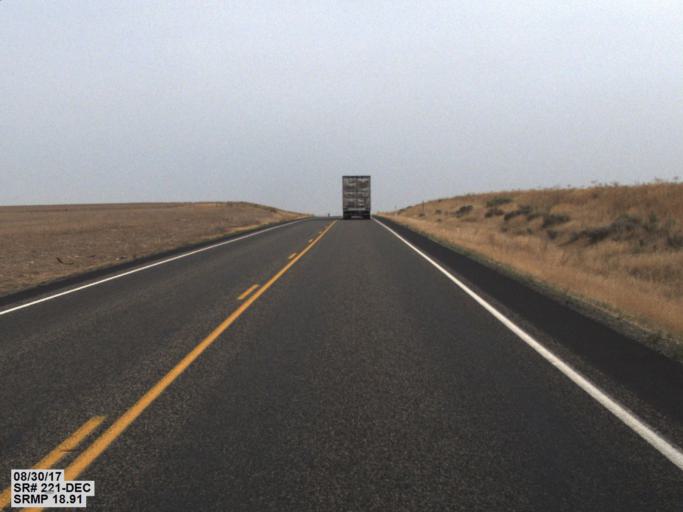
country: US
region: Washington
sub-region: Benton County
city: Prosser
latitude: 46.1868
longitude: -119.6350
